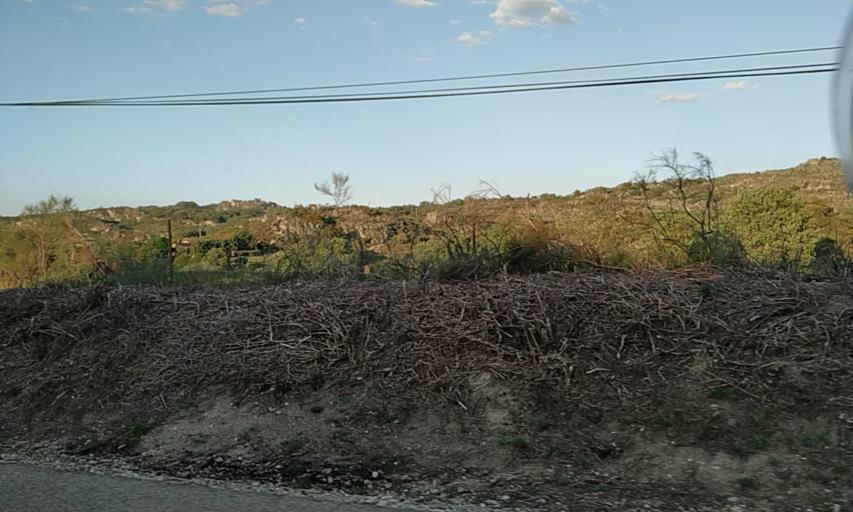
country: PT
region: Portalegre
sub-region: Portalegre
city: Sao Juliao
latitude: 39.3563
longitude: -7.2750
